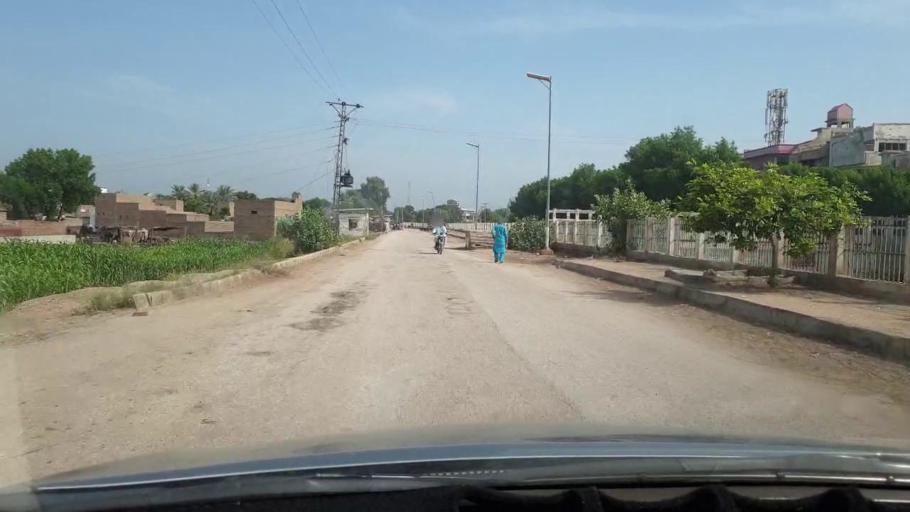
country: PK
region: Sindh
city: Khairpur
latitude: 27.5283
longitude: 68.7535
